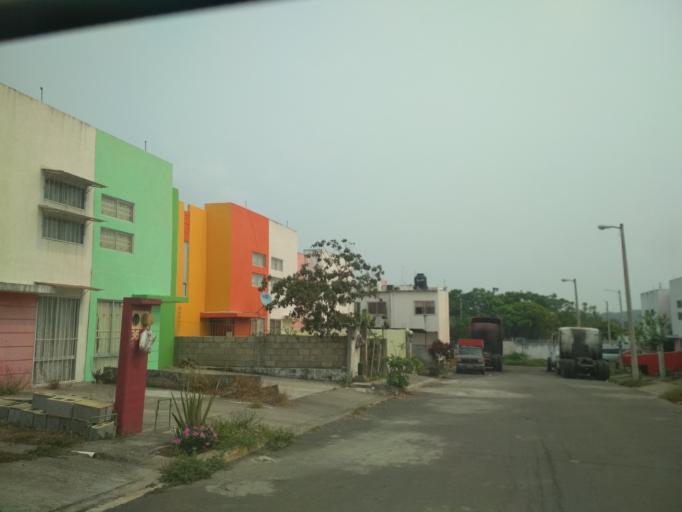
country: MX
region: Veracruz
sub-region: Veracruz
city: Fraccionamiento Geovillas los Pinos
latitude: 19.2314
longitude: -96.2411
